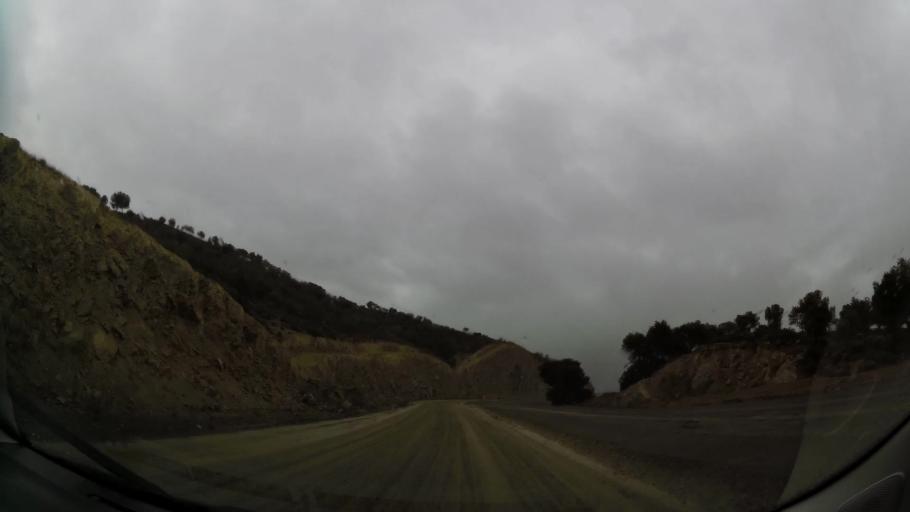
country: MA
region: Taza-Al Hoceima-Taounate
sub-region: Taza
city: Ajdir
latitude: 34.8998
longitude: -3.7854
